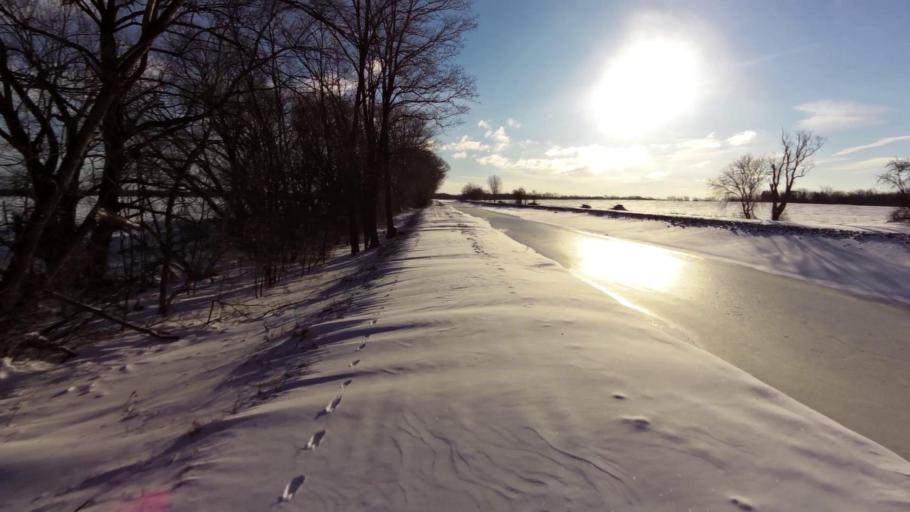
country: US
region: New York
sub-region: Orleans County
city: Albion
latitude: 43.2552
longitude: -78.2372
